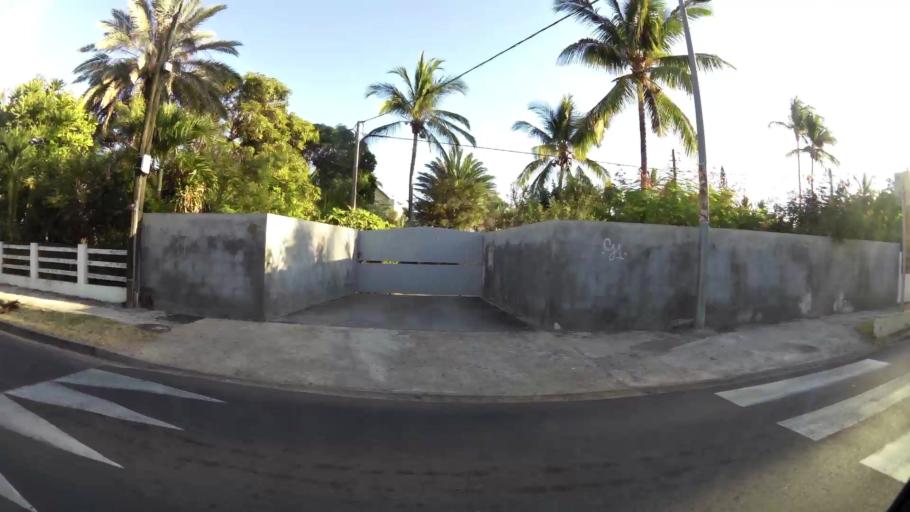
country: RE
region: Reunion
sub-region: Reunion
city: Trois-Bassins
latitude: -21.0972
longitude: 55.2402
